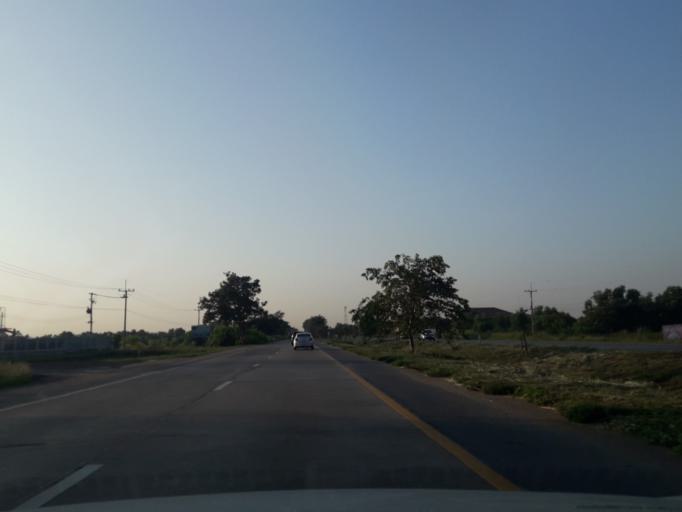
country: TH
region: Phra Nakhon Si Ayutthaya
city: Bang Pa-in
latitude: 14.2555
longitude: 100.5351
